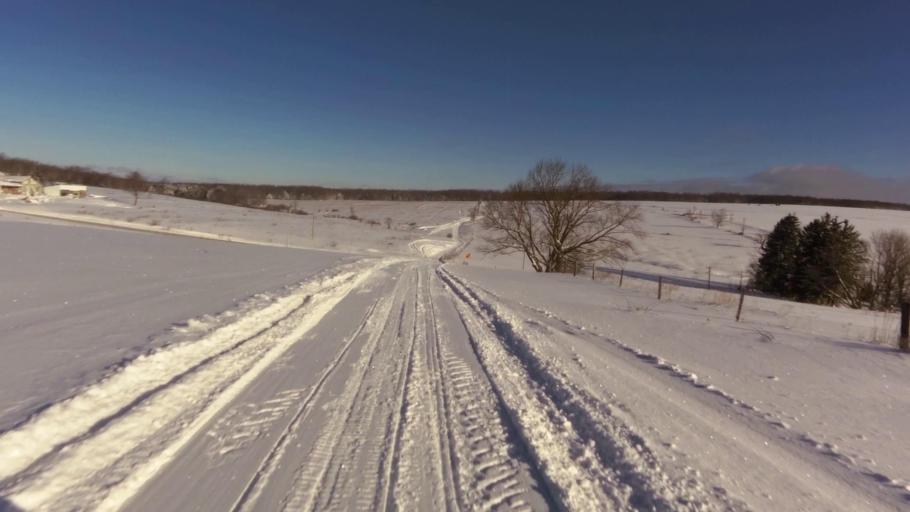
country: US
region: New York
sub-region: Chautauqua County
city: Falconer
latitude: 42.2599
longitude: -79.2030
